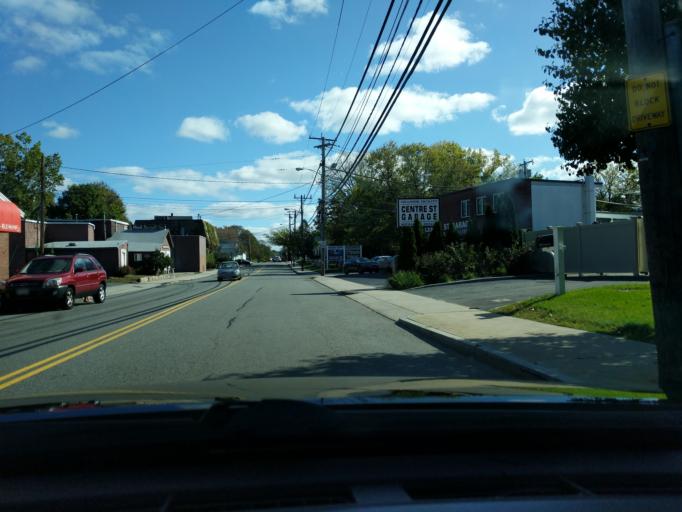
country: US
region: Massachusetts
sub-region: Norfolk County
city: Quincy
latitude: 42.2374
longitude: -71.0145
